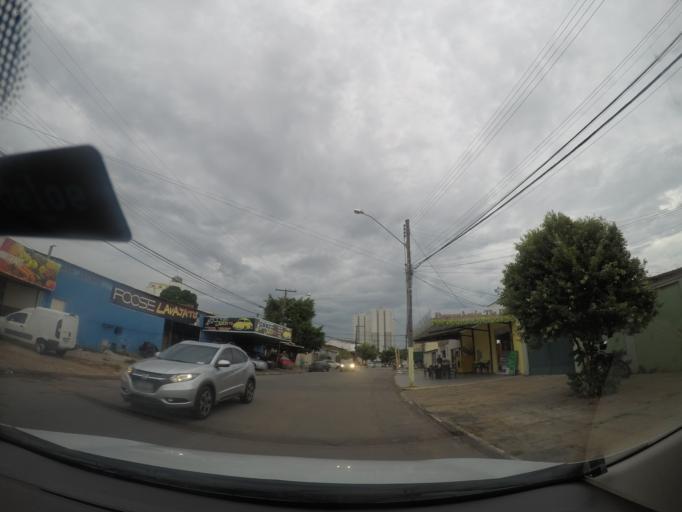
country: BR
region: Goias
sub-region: Goiania
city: Goiania
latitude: -16.6564
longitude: -49.2424
